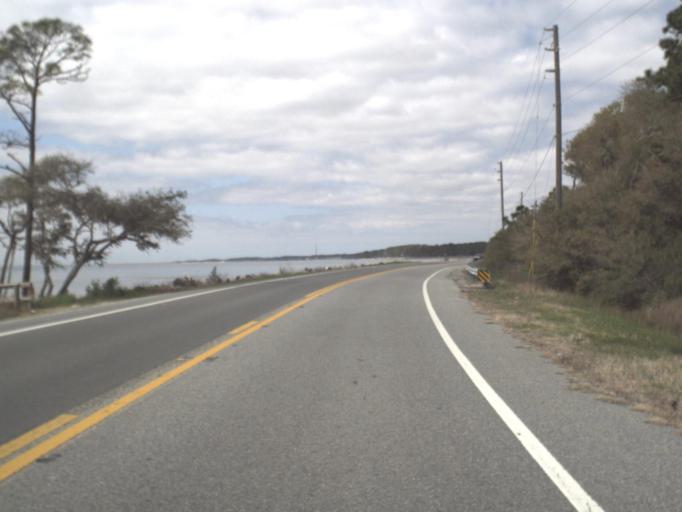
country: US
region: Florida
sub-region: Franklin County
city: Eastpoint
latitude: 29.7586
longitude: -84.8243
